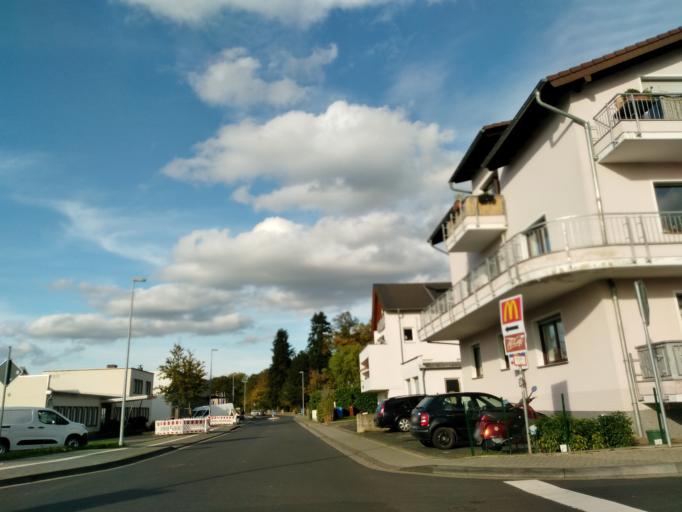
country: DE
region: Rheinland-Pfalz
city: Rheinbreitbach
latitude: 50.6241
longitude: 7.2297
